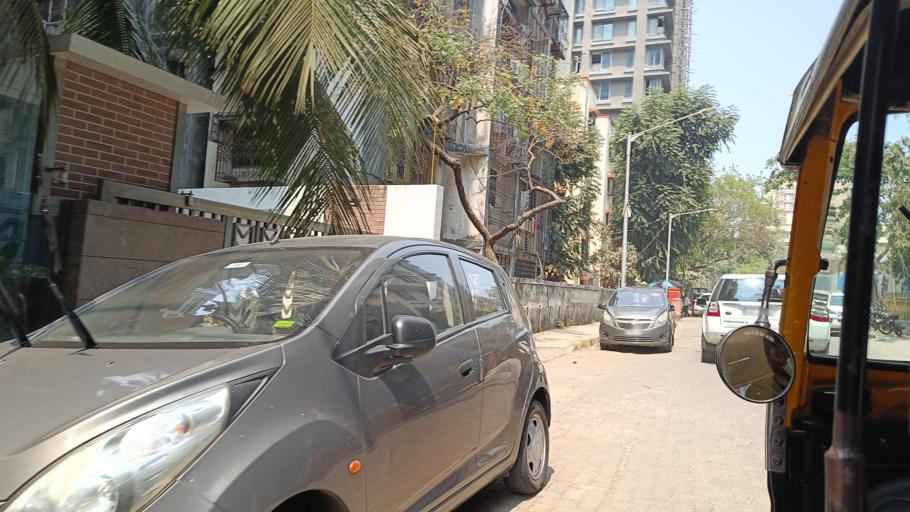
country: IN
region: Maharashtra
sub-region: Mumbai Suburban
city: Mumbai
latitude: 19.1130
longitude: 72.8309
